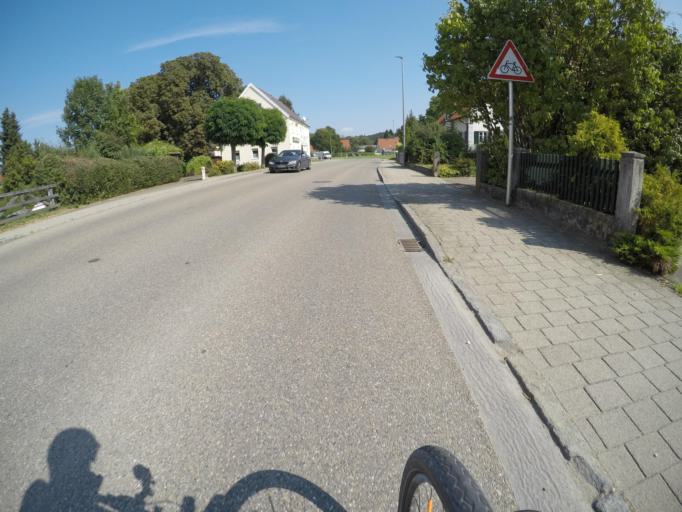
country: DE
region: Bavaria
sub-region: Swabia
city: Binswangen
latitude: 48.5611
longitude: 10.6470
